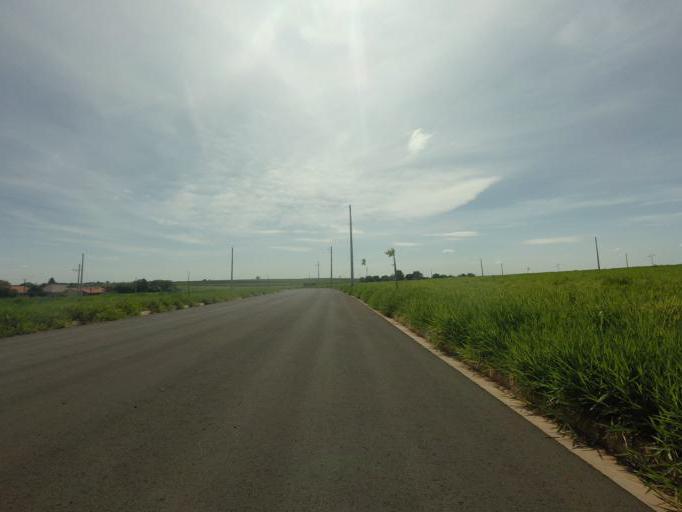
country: BR
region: Sao Paulo
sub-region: Piracicaba
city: Piracicaba
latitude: -22.7597
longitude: -47.5805
